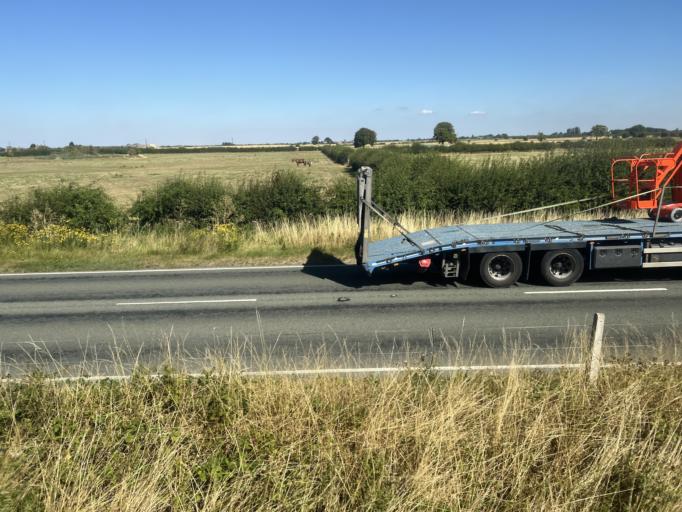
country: GB
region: England
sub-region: Lincolnshire
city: Donington
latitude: 52.9722
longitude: -0.1671
